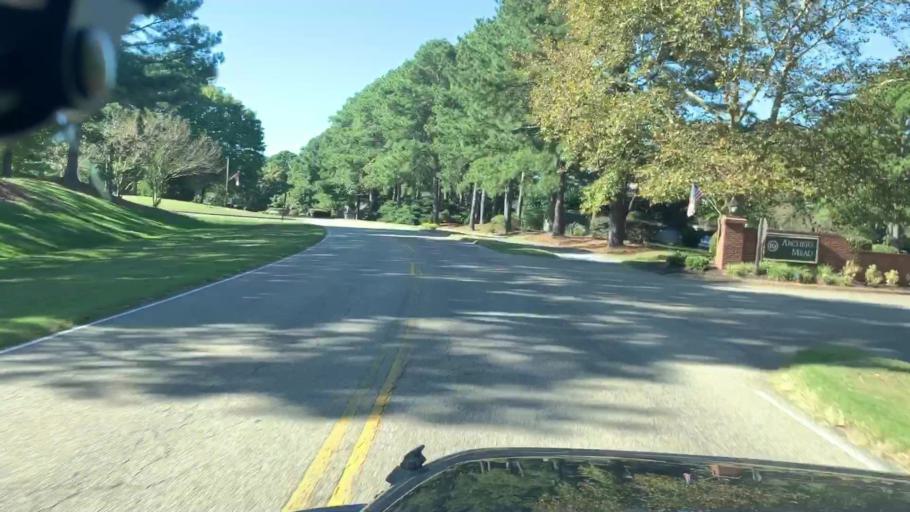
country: US
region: Virginia
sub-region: City of Williamsburg
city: Williamsburg
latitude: 37.2321
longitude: -76.6683
